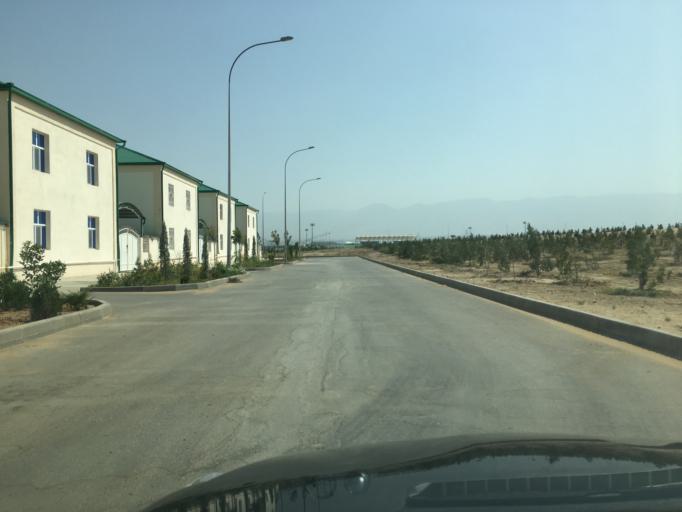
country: TM
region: Ahal
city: Ashgabat
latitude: 38.0043
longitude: 58.3951
